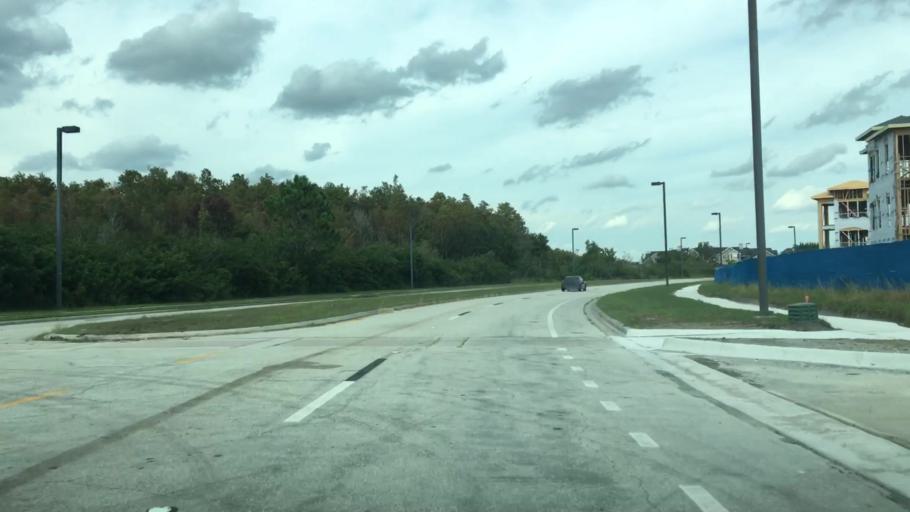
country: US
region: Florida
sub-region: Orange County
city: Conway
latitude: 28.4697
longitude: -81.2985
